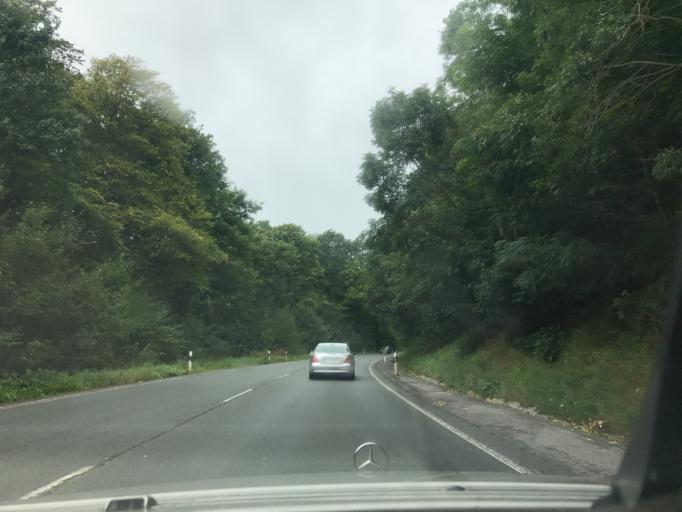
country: DE
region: North Rhine-Westphalia
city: Wetter (Ruhr)
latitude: 51.3496
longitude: 7.4037
